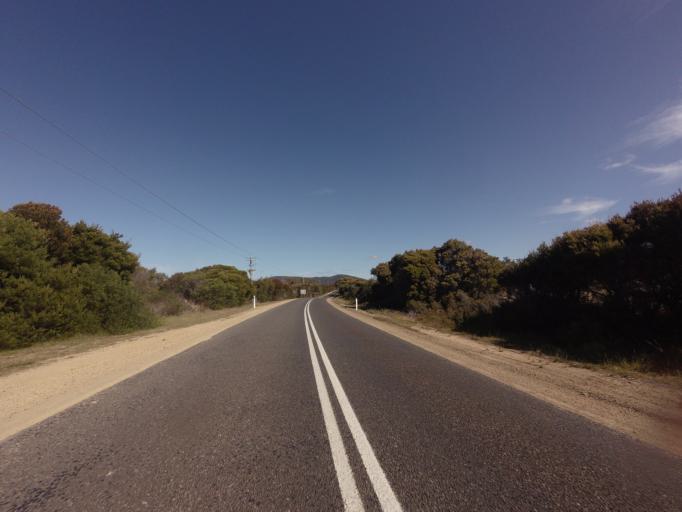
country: AU
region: Tasmania
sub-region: Break O'Day
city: St Helens
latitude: -41.8220
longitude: 148.2632
